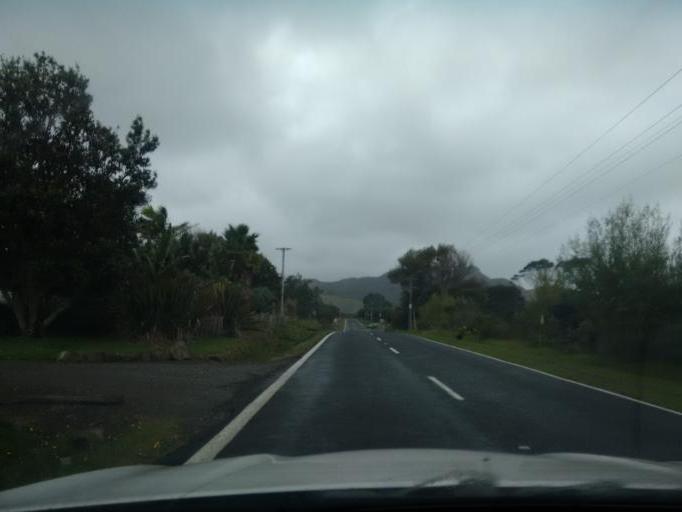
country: NZ
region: Waikato
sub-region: Thames-Coromandel District
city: Whitianga
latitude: -36.8013
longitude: 175.7196
